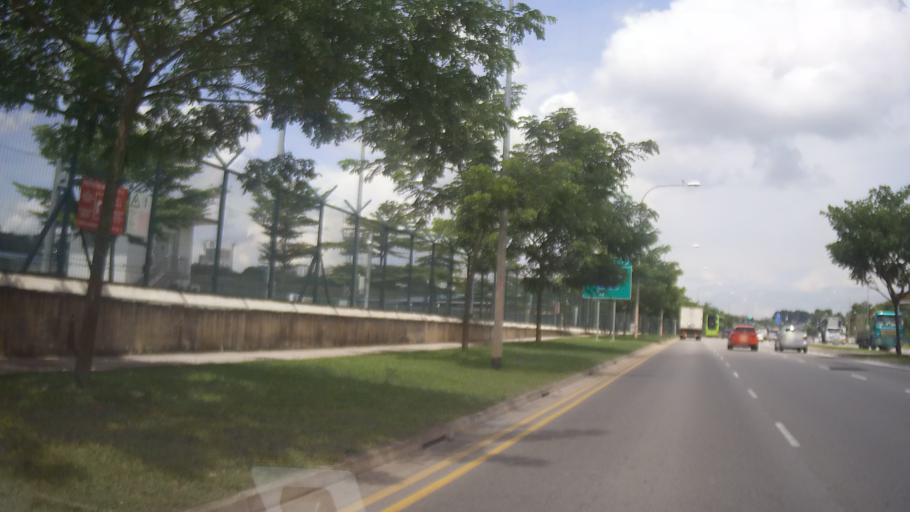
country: MY
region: Johor
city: Johor Bahru
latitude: 1.4005
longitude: 103.7557
